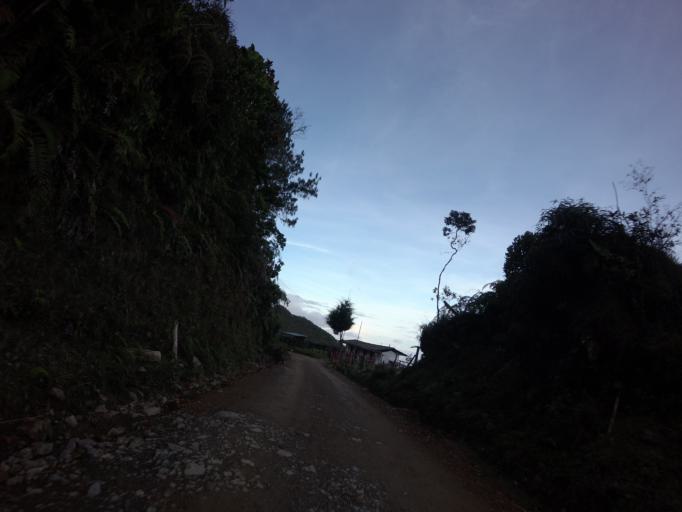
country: CO
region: Caldas
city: Pensilvania
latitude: 5.4520
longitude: -75.1245
